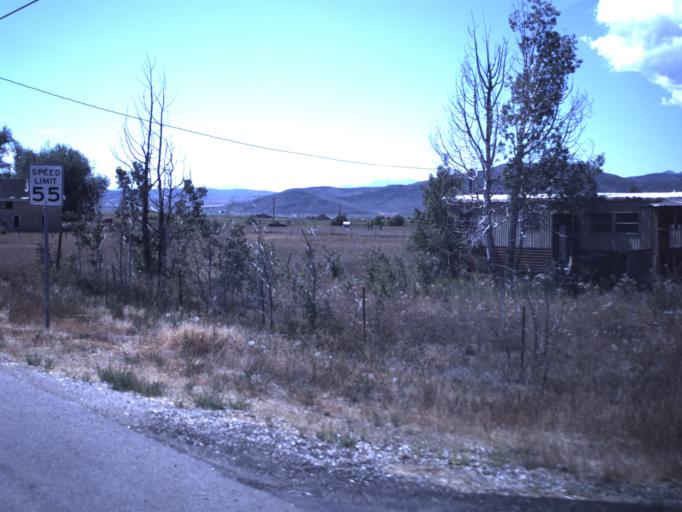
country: US
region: Utah
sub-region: Summit County
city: Oakley
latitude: 40.7011
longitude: -111.2811
